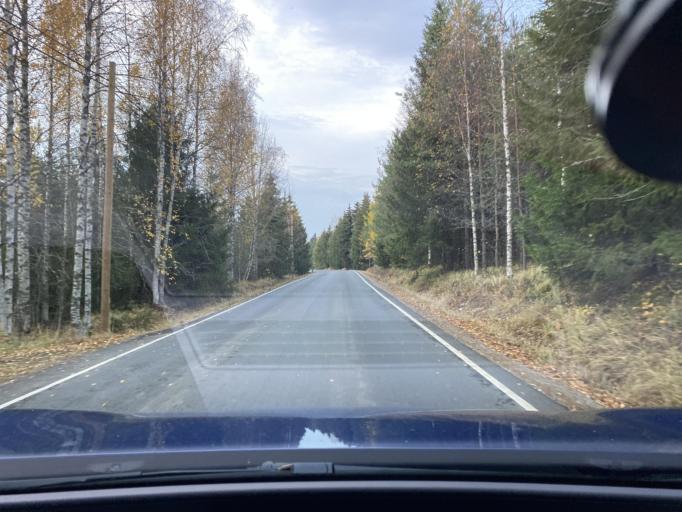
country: FI
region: Varsinais-Suomi
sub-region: Loimaa
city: Alastaro
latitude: 61.0898
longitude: 22.9101
